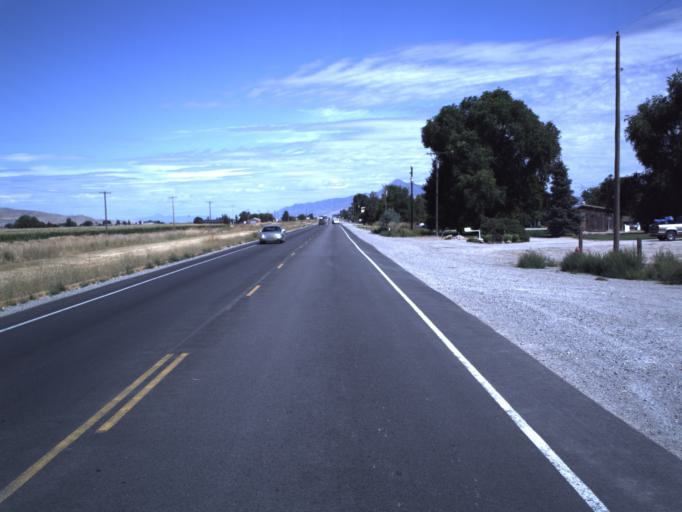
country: US
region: Utah
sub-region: Box Elder County
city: Elwood
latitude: 41.6913
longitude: -112.1416
